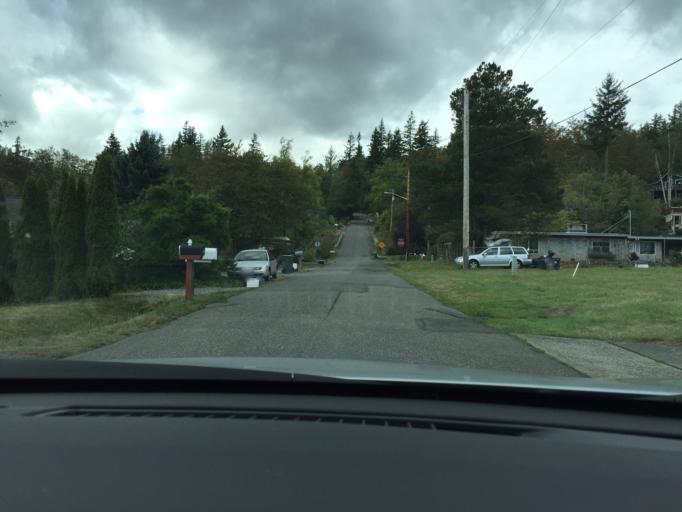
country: US
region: Washington
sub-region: Whatcom County
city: Geneva
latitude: 48.7700
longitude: -122.4110
